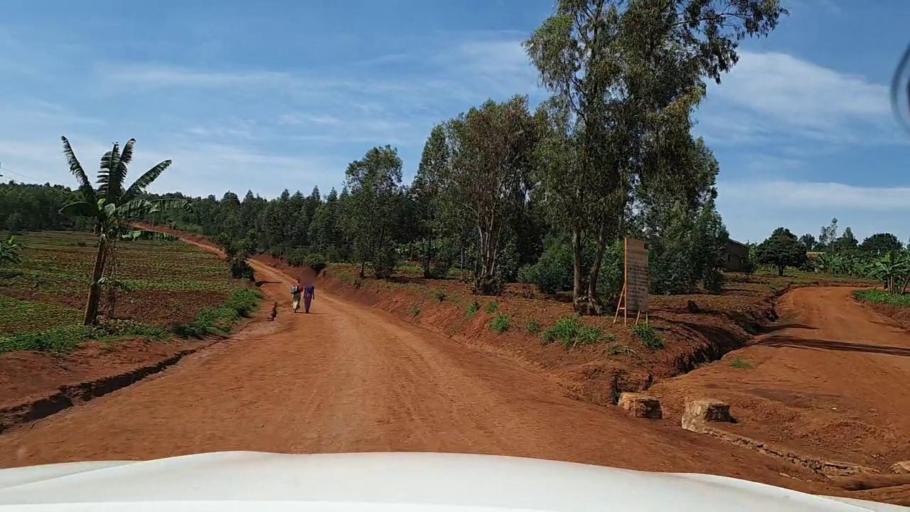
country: RW
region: Southern Province
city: Butare
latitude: -2.6997
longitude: 29.8540
